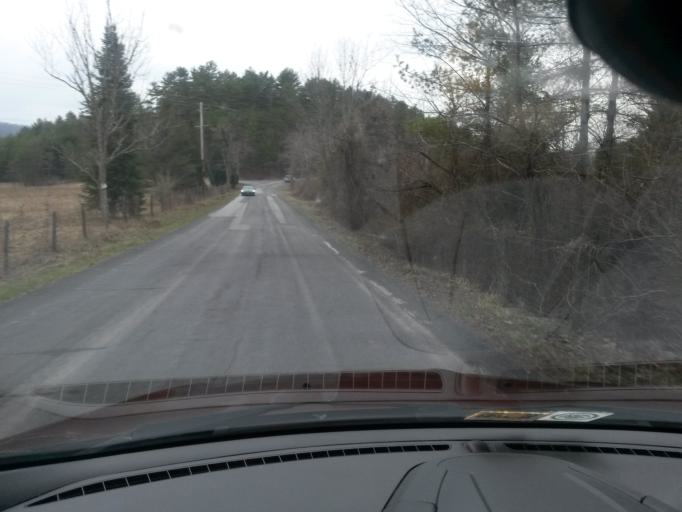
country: US
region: Virginia
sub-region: Bath County
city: Warm Springs
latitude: 38.0369
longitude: -79.8577
